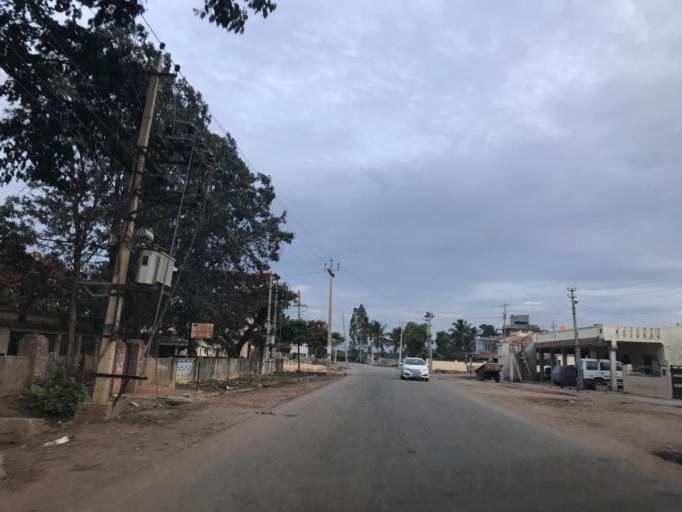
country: IN
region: Karnataka
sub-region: Bangalore Rural
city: Devanhalli
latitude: 13.1615
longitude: 77.7241
